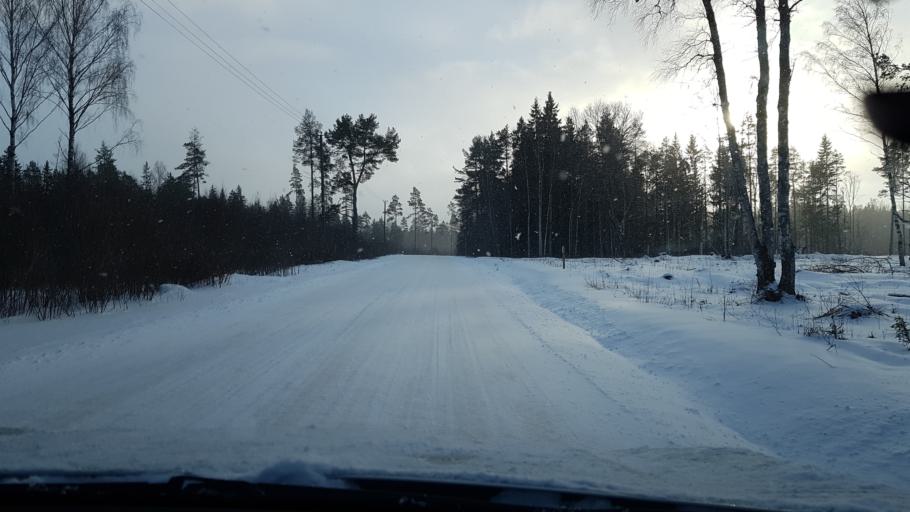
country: EE
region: Harju
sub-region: Nissi vald
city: Turba
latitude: 59.1956
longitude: 24.1395
